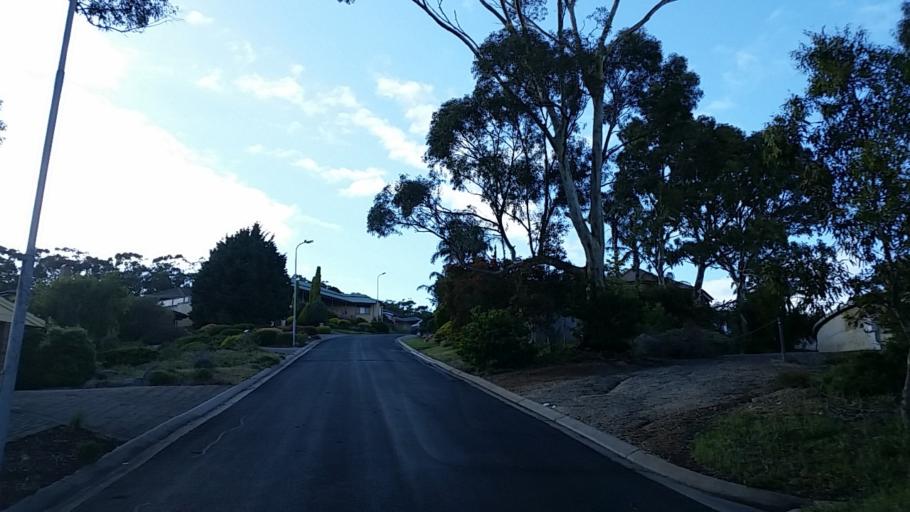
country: AU
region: South Australia
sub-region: Mitcham
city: Clapham
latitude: -35.0111
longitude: 138.5929
